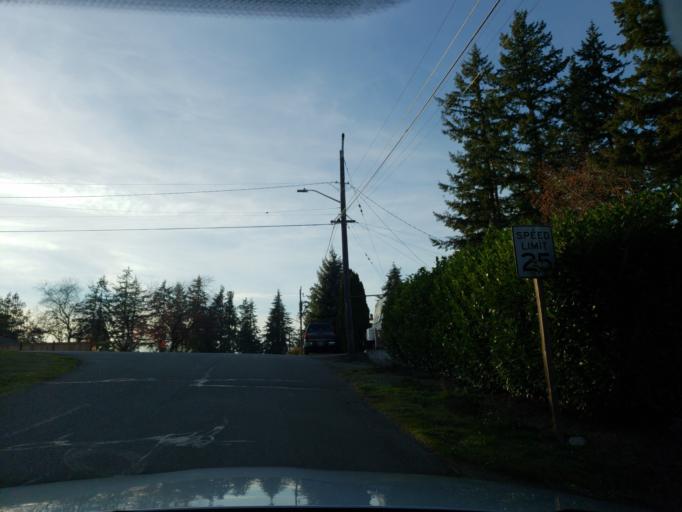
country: US
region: Washington
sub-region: King County
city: Shoreline
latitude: 47.7626
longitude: -122.3562
